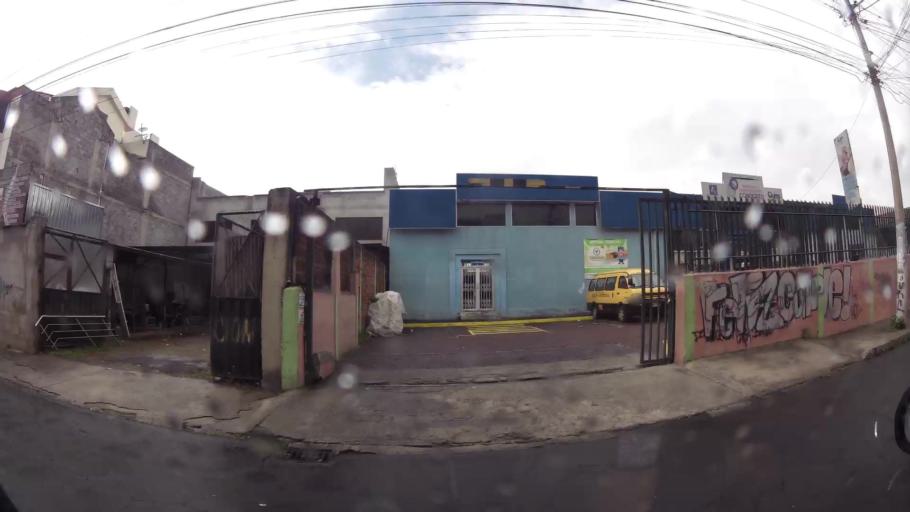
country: EC
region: Pichincha
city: Sangolqui
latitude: -0.2973
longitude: -78.4804
